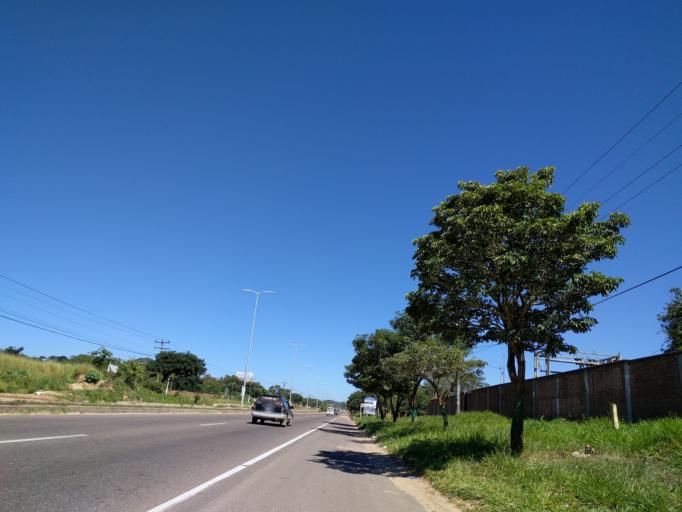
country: BO
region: Santa Cruz
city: Santa Rita
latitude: -17.8736
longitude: -63.2781
